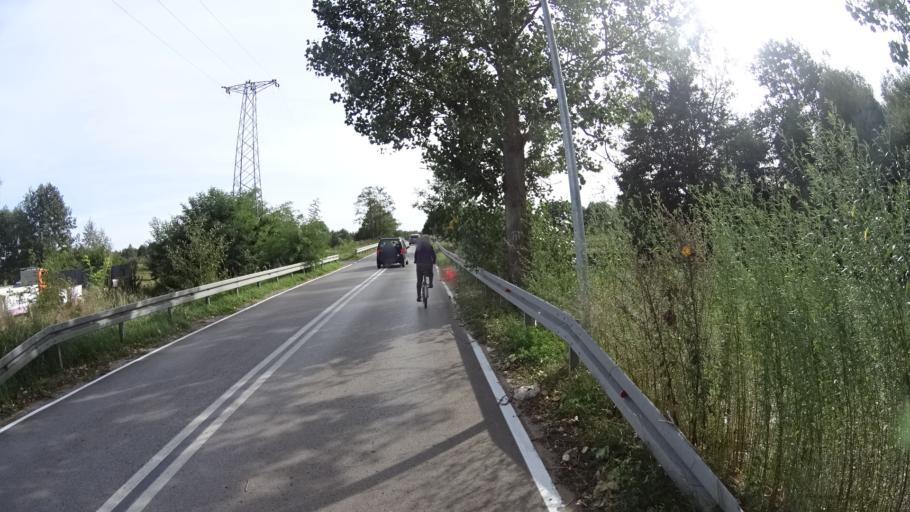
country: PL
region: Masovian Voivodeship
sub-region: Powiat legionowski
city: Serock
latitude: 52.4781
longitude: 21.0925
